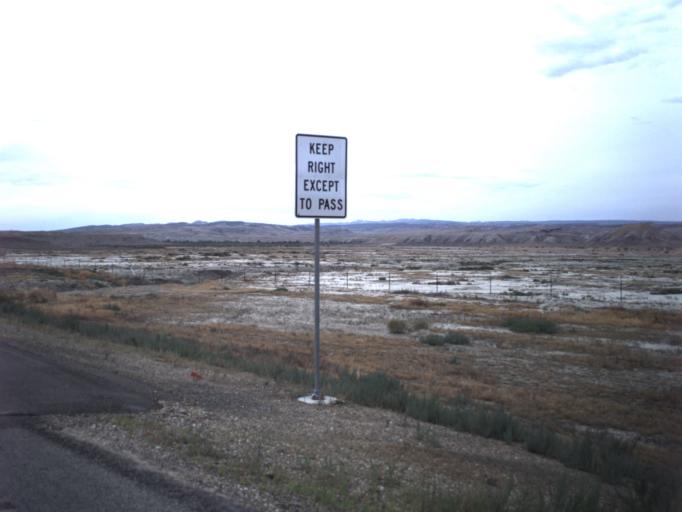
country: US
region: Utah
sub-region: Carbon County
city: East Carbon City
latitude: 39.3244
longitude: -110.3662
